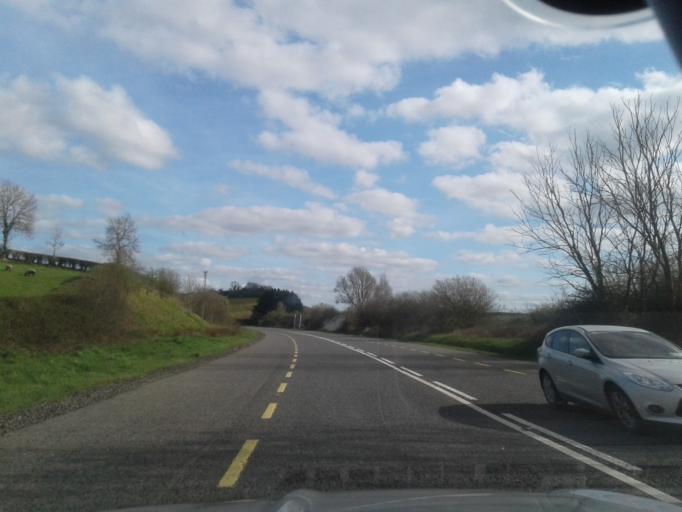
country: IE
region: Ulster
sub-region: County Monaghan
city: Carrickmacross
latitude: 53.9279
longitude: -6.6462
